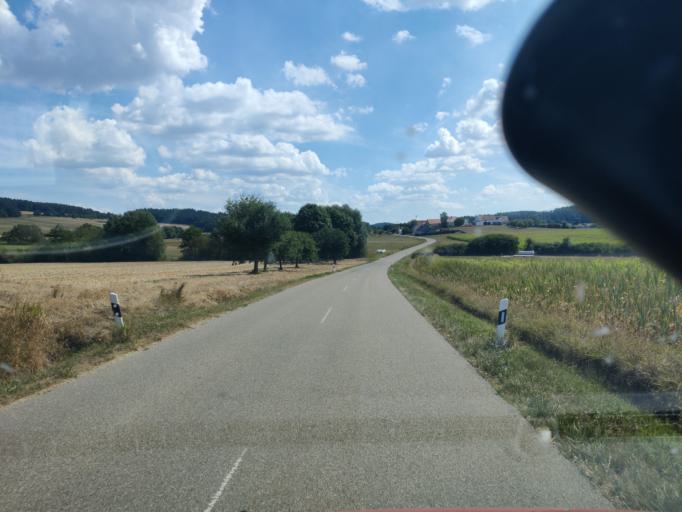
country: DE
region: Bavaria
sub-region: Regierungsbezirk Mittelfranken
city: Thalmassing
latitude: 49.1072
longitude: 11.2083
